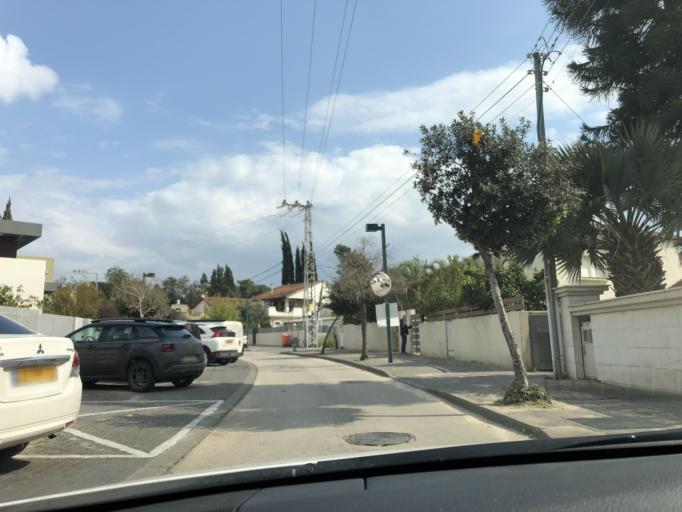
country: IL
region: Central District
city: Ganne Tiqwa
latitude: 32.0567
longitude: 34.8715
